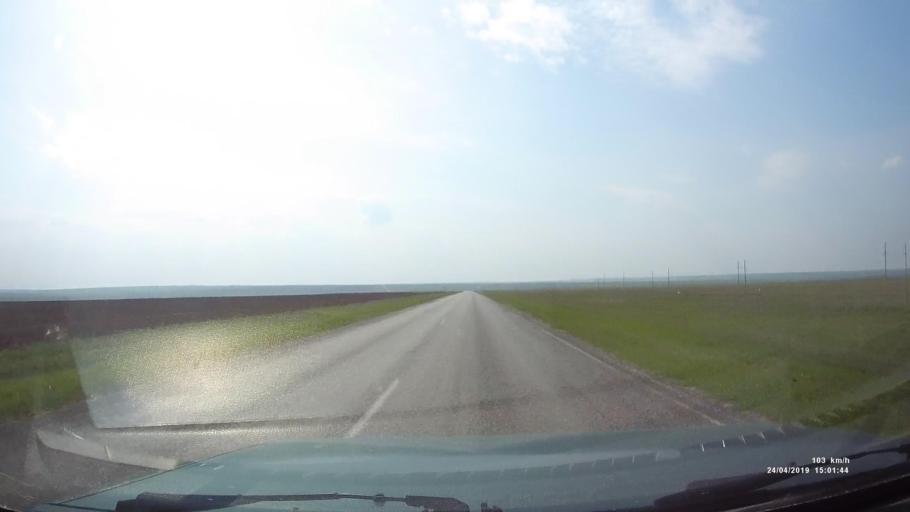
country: RU
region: Rostov
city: Remontnoye
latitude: 46.5664
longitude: 43.5274
